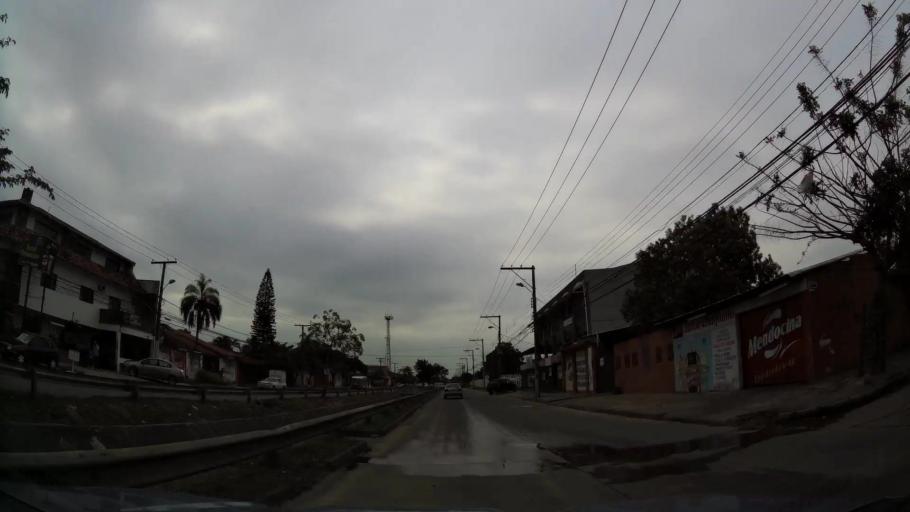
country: BO
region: Santa Cruz
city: Santa Cruz de la Sierra
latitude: -17.7558
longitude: -63.1819
